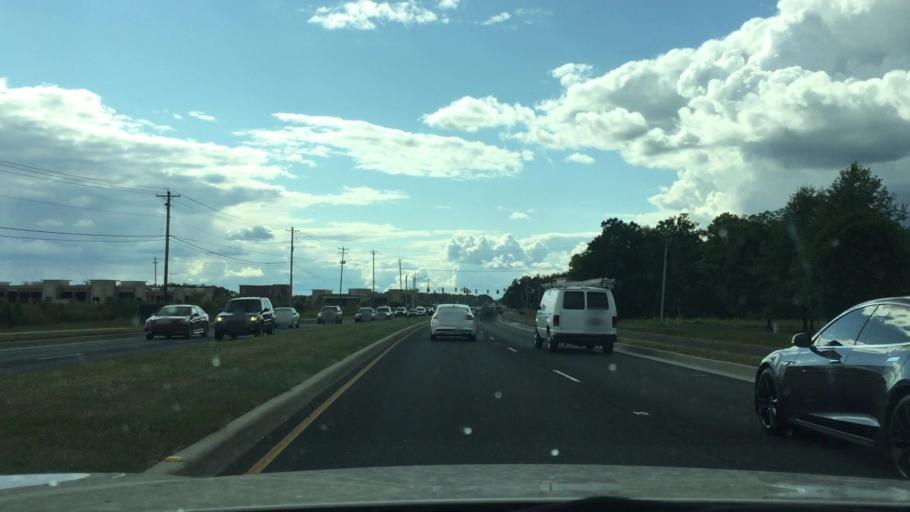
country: US
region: Indiana
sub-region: Hamilton County
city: Fishers
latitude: 40.0001
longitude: -86.0304
